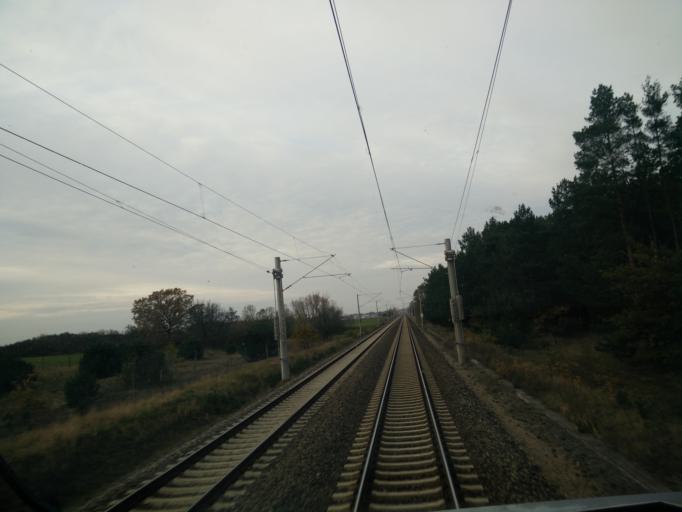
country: DE
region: Brandenburg
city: Luebben
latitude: 51.9145
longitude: 13.8984
